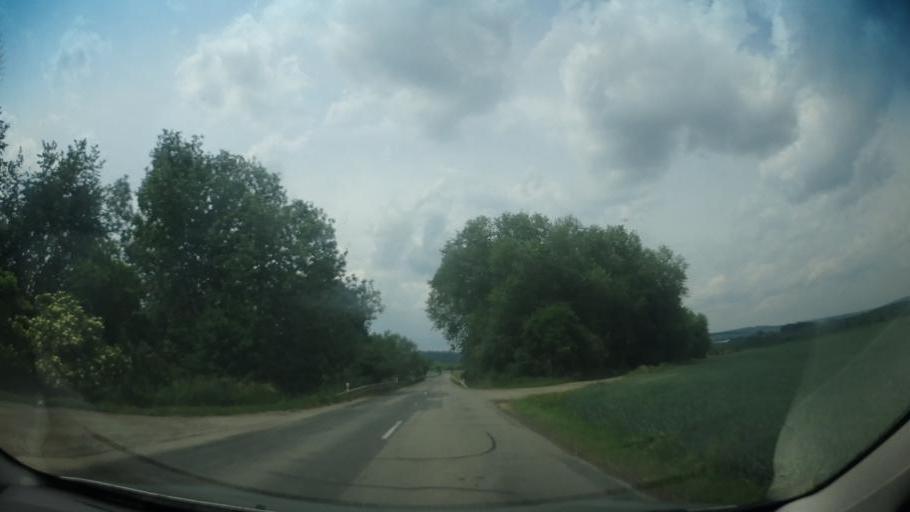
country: CZ
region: South Moravian
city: Lysice
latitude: 49.4405
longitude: 16.5591
